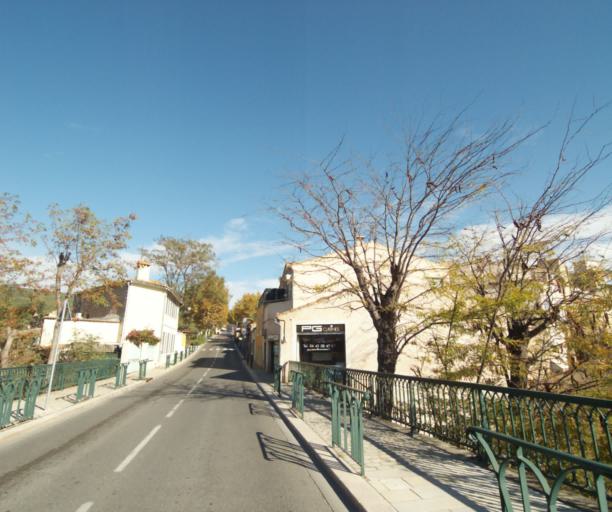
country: FR
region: Provence-Alpes-Cote d'Azur
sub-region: Departement des Bouches-du-Rhone
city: Ceyreste
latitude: 43.2133
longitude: 5.6301
